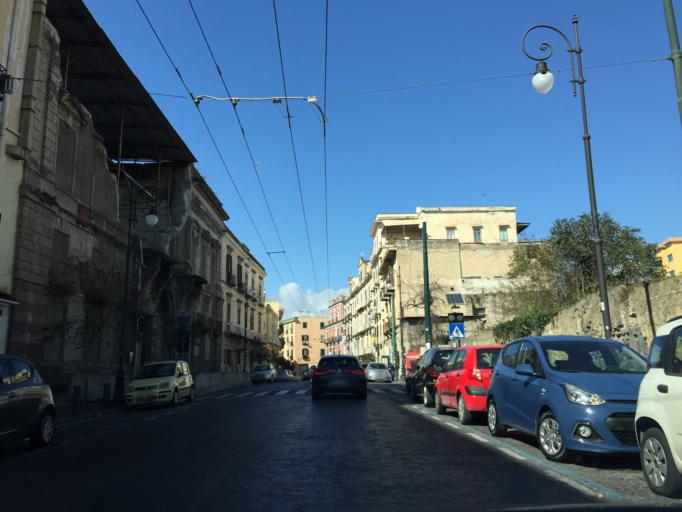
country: IT
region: Campania
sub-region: Provincia di Napoli
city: Portici
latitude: 40.8200
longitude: 14.3280
